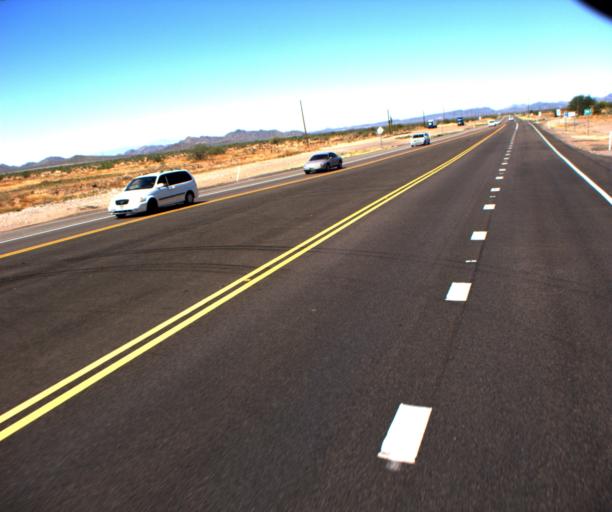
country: US
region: Arizona
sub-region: Maricopa County
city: Anthem
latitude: 33.7983
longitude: -112.1395
